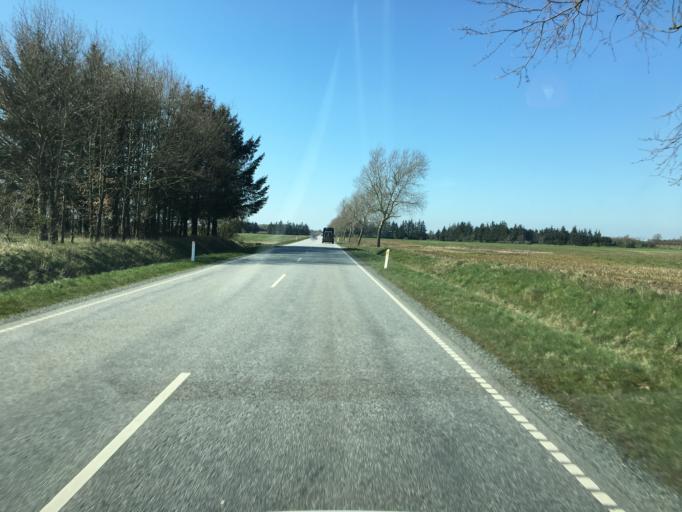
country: DK
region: South Denmark
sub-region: Aabenraa Kommune
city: Tinglev
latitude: 54.9471
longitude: 9.3515
